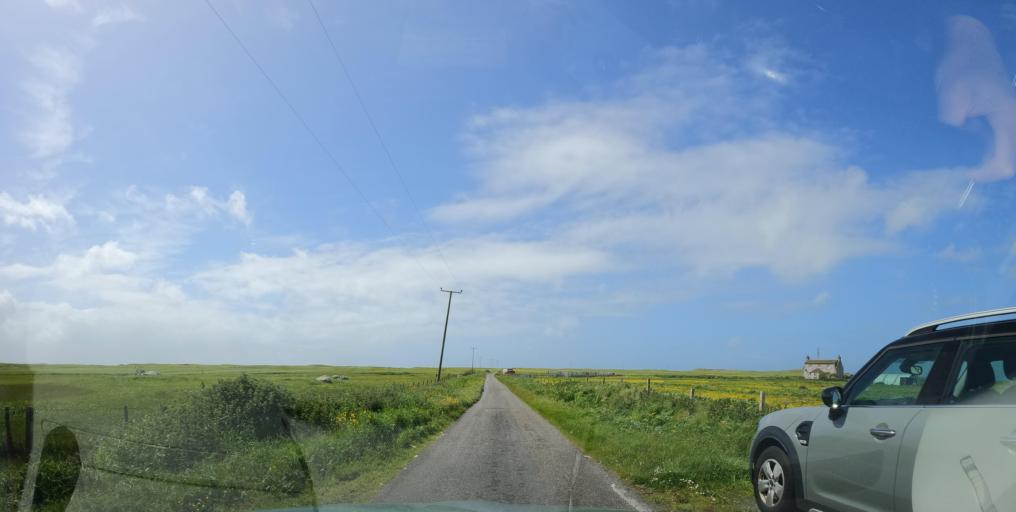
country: GB
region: Scotland
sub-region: Eilean Siar
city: Isle of South Uist
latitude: 57.1642
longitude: -7.3939
